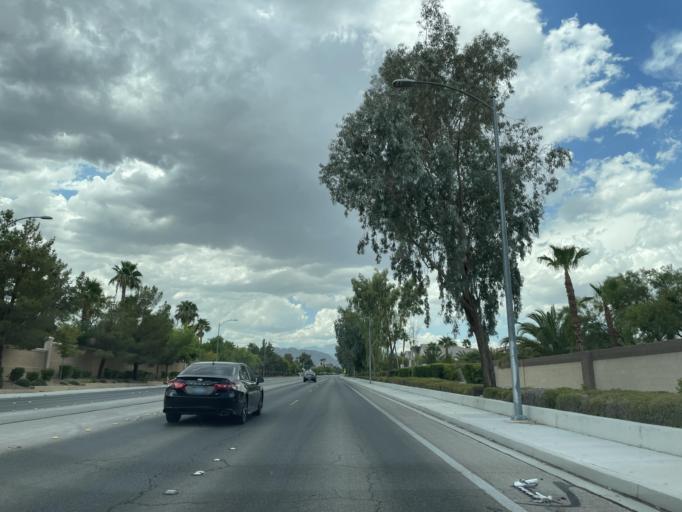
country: US
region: Nevada
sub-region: Clark County
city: North Las Vegas
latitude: 36.2979
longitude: -115.2563
